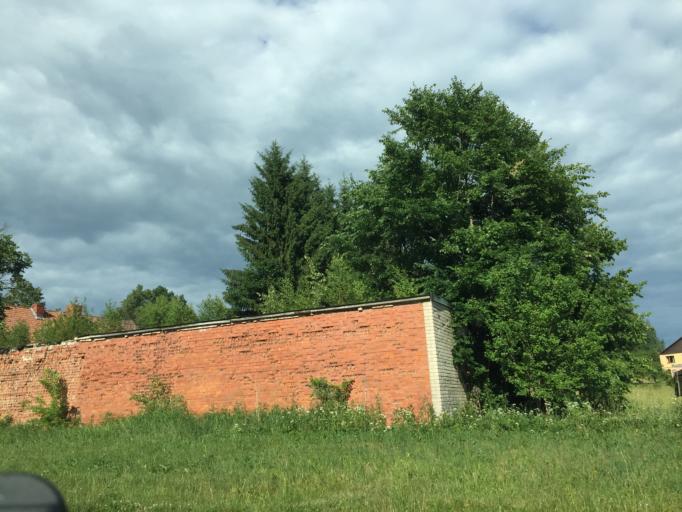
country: LV
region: Skriveri
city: Skriveri
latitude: 56.8467
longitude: 25.1506
